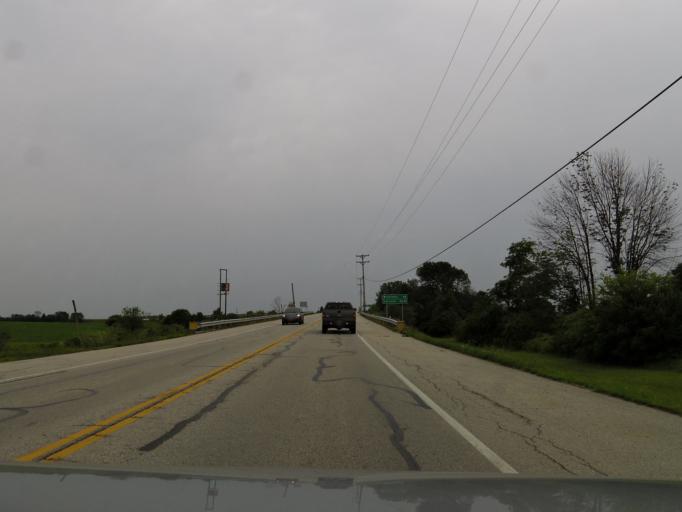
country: US
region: Ohio
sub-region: Clinton County
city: Wilmington
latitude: 39.4866
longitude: -83.9462
